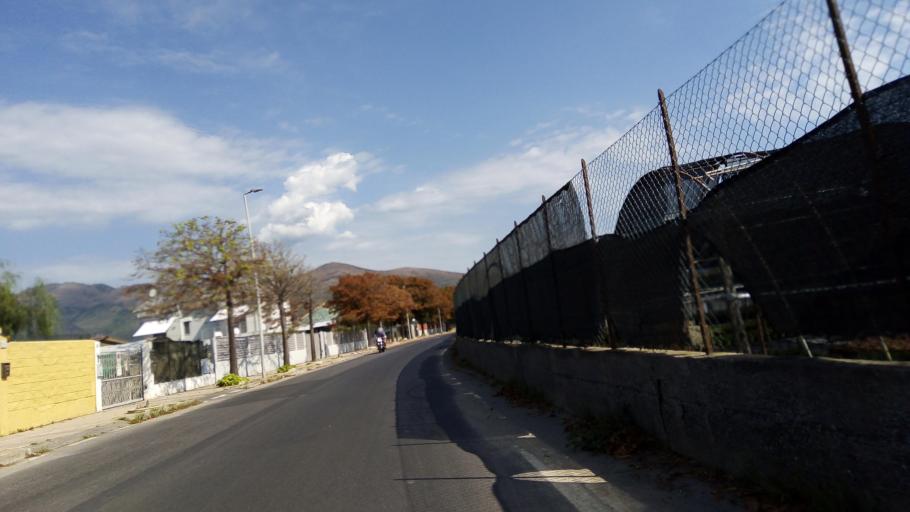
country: IT
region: Liguria
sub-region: Provincia di Savona
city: Ceriale
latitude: 44.0702
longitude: 8.2252
